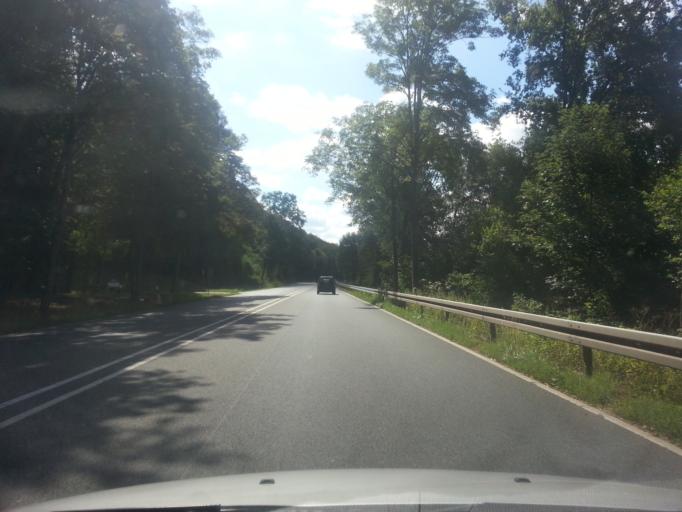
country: DE
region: Hesse
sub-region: Regierungsbezirk Darmstadt
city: Bad Konig
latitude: 49.7661
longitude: 8.9946
